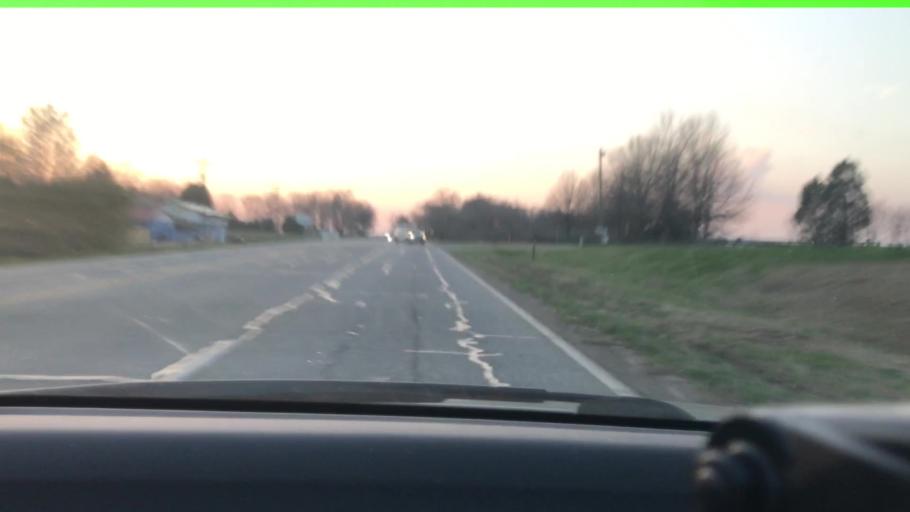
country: US
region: Georgia
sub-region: Oglethorpe County
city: Lexington
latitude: 33.8904
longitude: -83.1905
